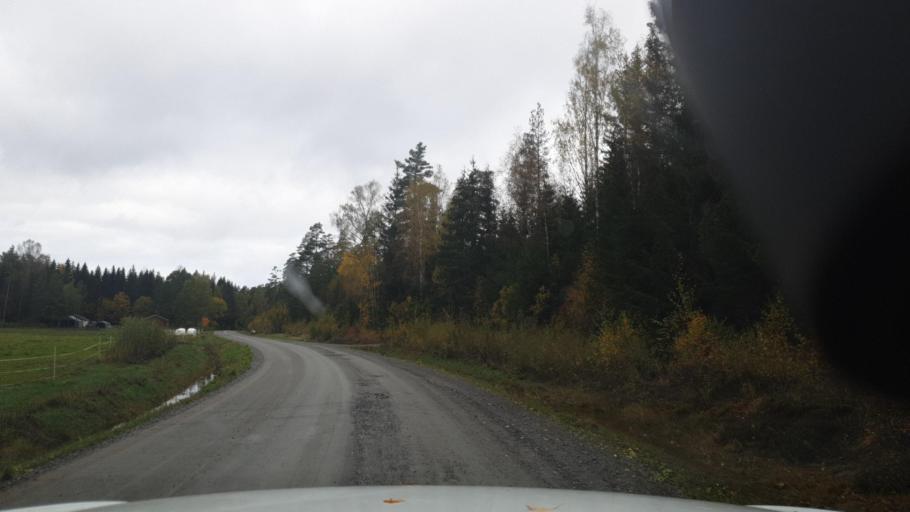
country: SE
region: Vaermland
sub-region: Karlstads Kommun
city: Edsvalla
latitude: 59.4494
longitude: 13.1533
